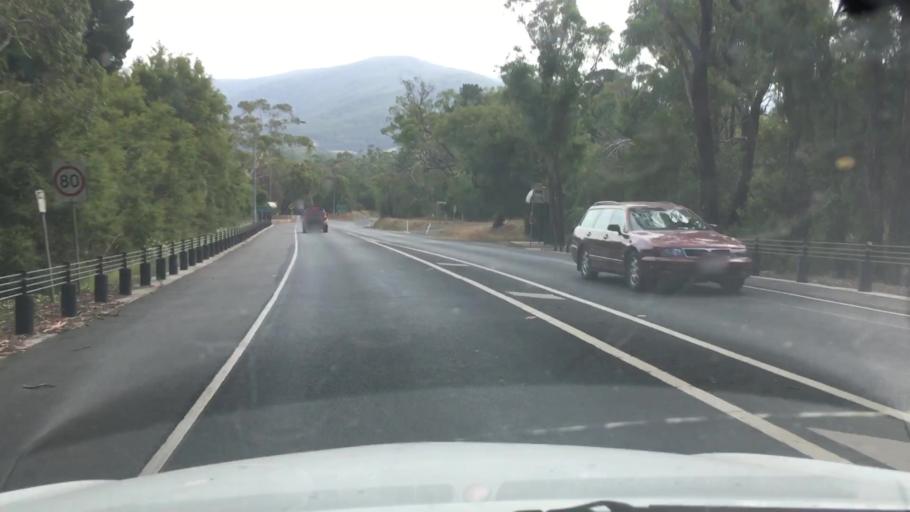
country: AU
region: Victoria
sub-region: Yarra Ranges
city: Launching Place
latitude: -37.7780
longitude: 145.5726
